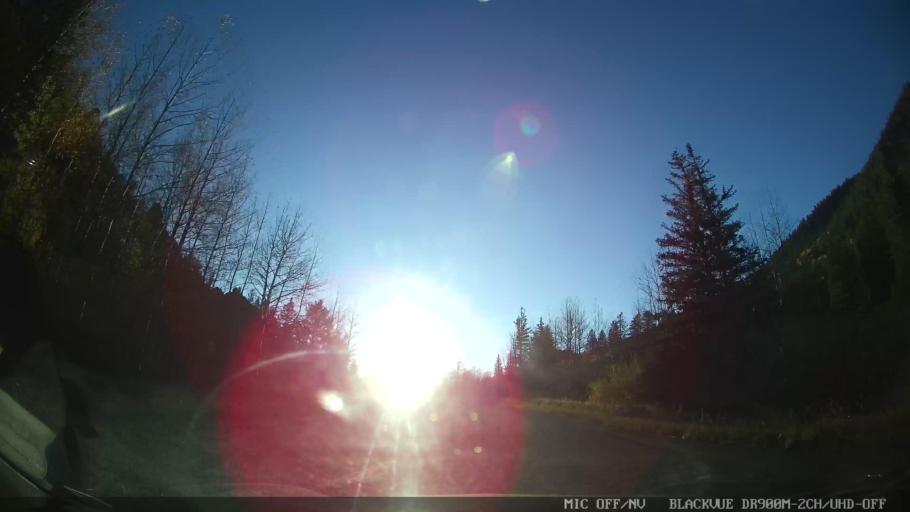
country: US
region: Colorado
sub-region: Grand County
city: Kremmling
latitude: 39.9943
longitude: -106.4729
